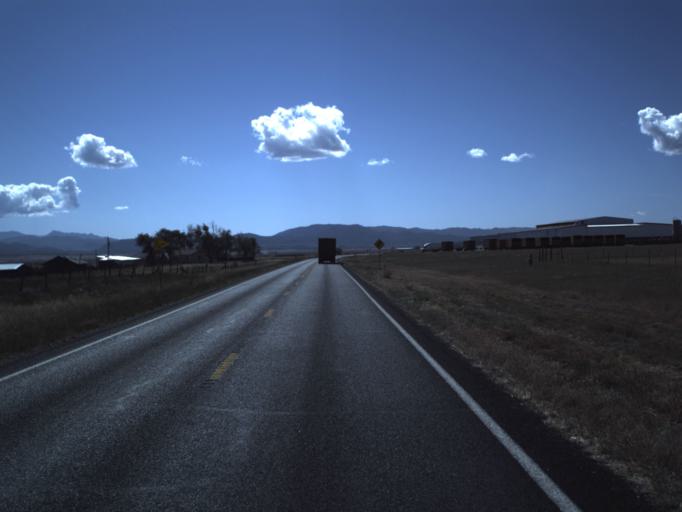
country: US
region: Utah
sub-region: Washington County
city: Enterprise
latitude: 37.6810
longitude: -113.6565
